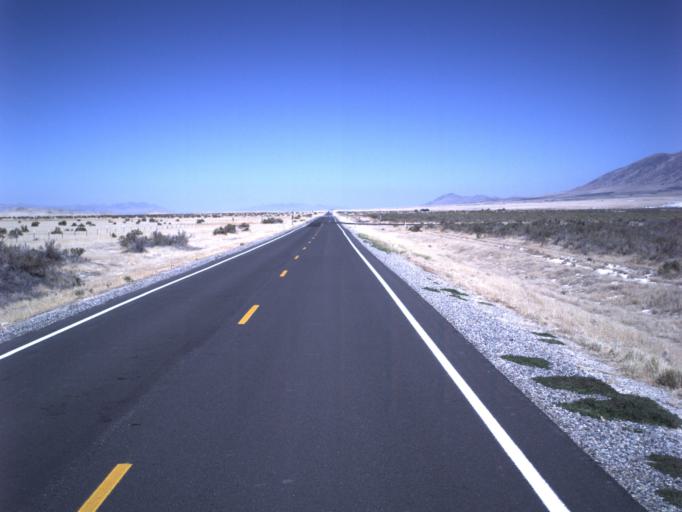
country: US
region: Utah
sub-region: Tooele County
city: Grantsville
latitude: 40.3049
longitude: -112.7430
